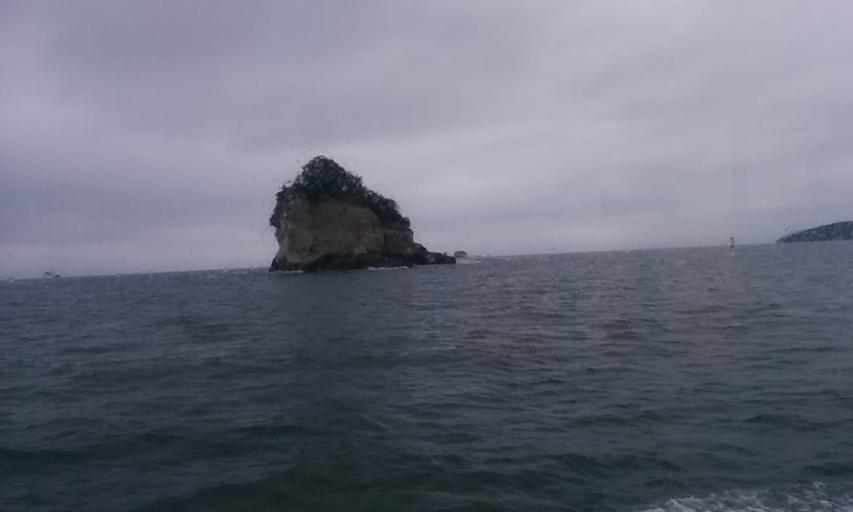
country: JP
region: Miyagi
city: Matsushima
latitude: 38.3228
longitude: 141.1016
